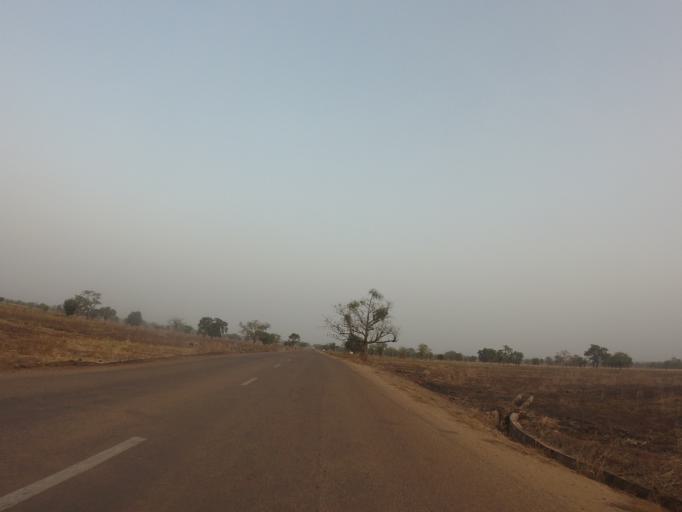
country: GH
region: Northern
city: Tamale
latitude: 9.4429
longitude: -1.1090
